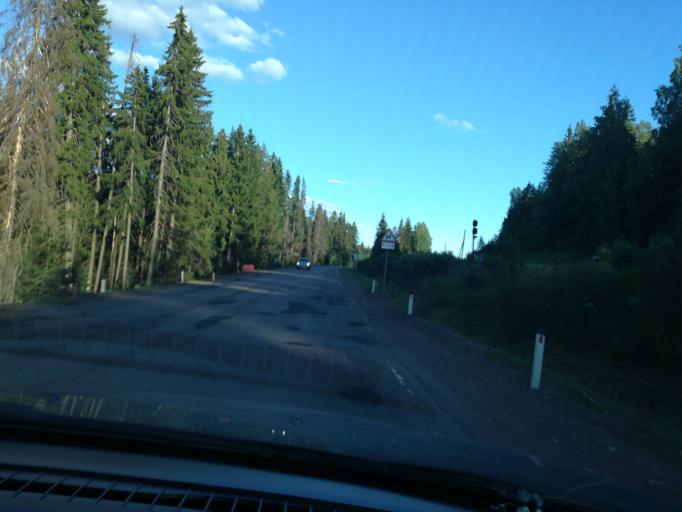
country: RU
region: Leningrad
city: Lesogorskiy
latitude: 61.0572
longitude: 28.9209
